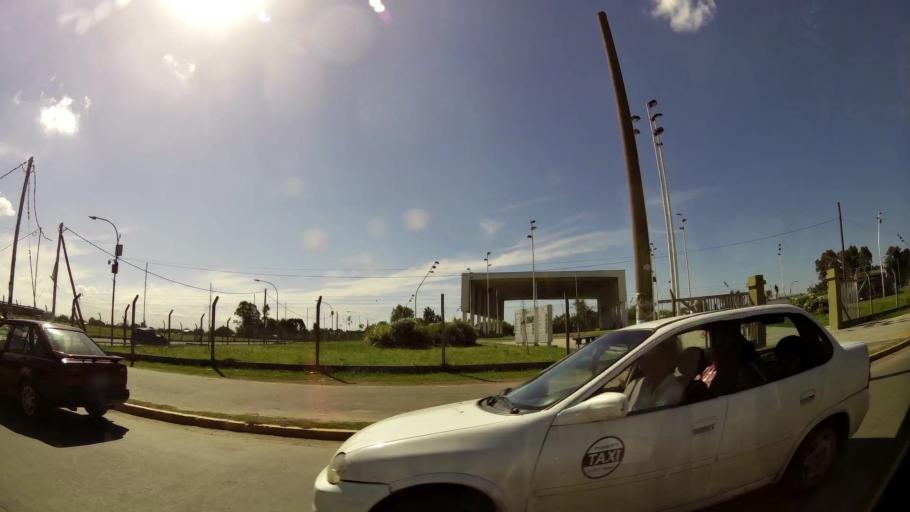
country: AR
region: Buenos Aires
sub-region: Partido de Quilmes
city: Quilmes
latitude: -34.7940
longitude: -58.2525
